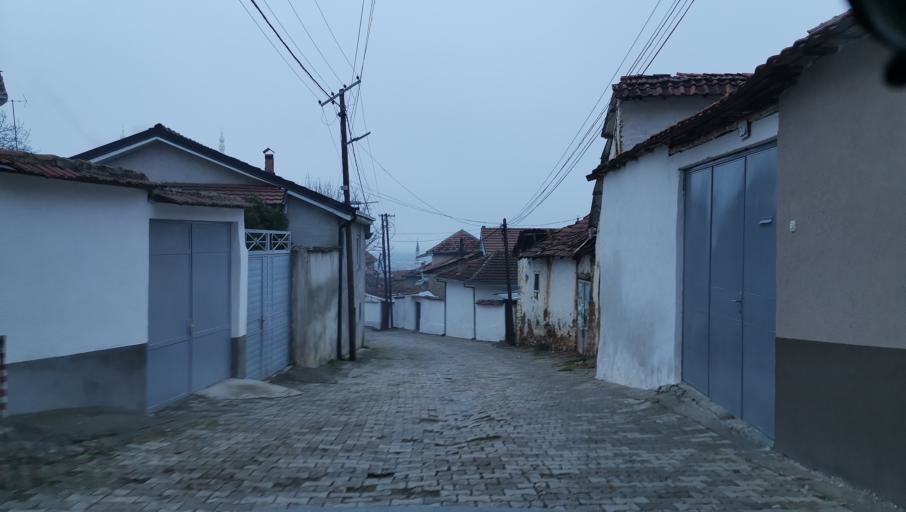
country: MK
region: Debar
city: Debar
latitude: 41.5278
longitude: 20.5285
